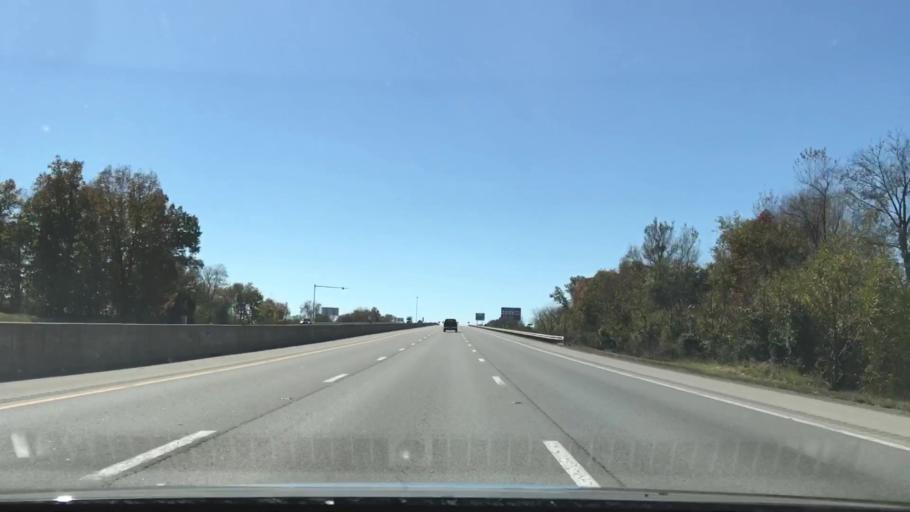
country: US
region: Kentucky
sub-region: Simpson County
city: Franklin
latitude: 36.6768
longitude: -86.5469
